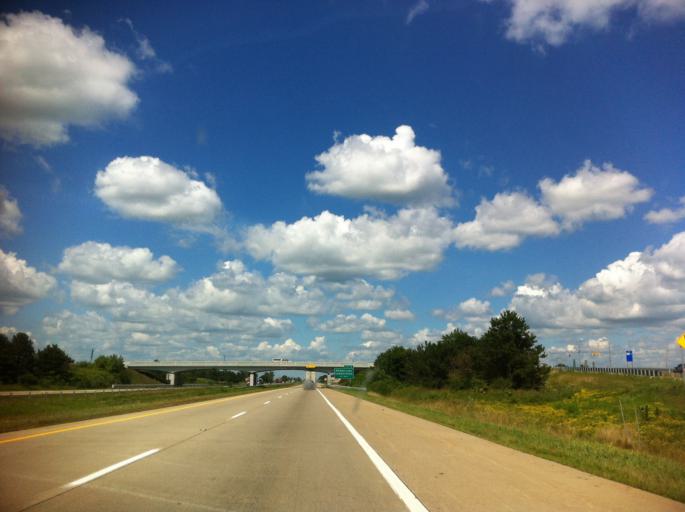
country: US
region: Ohio
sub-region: Lucas County
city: Sylvania
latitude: 41.7455
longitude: -83.6938
